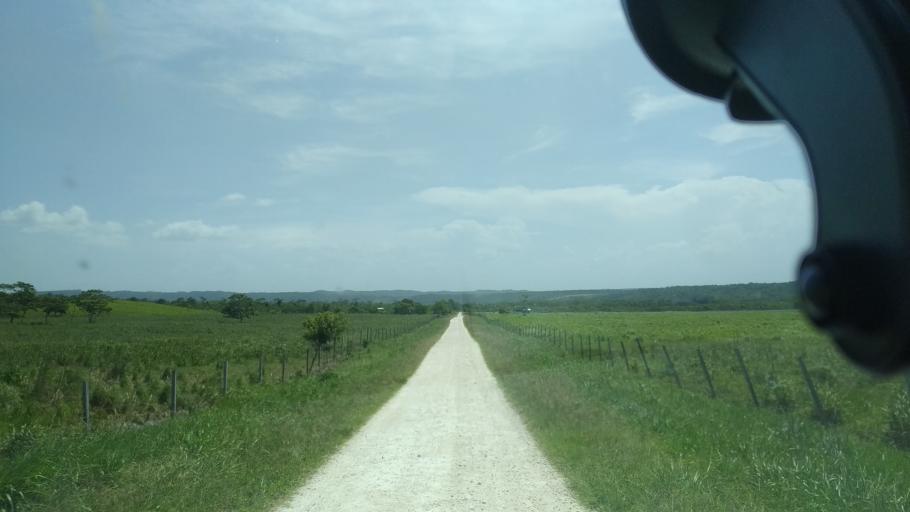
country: BZ
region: Cayo
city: San Ignacio
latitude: 17.2899
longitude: -89.0757
